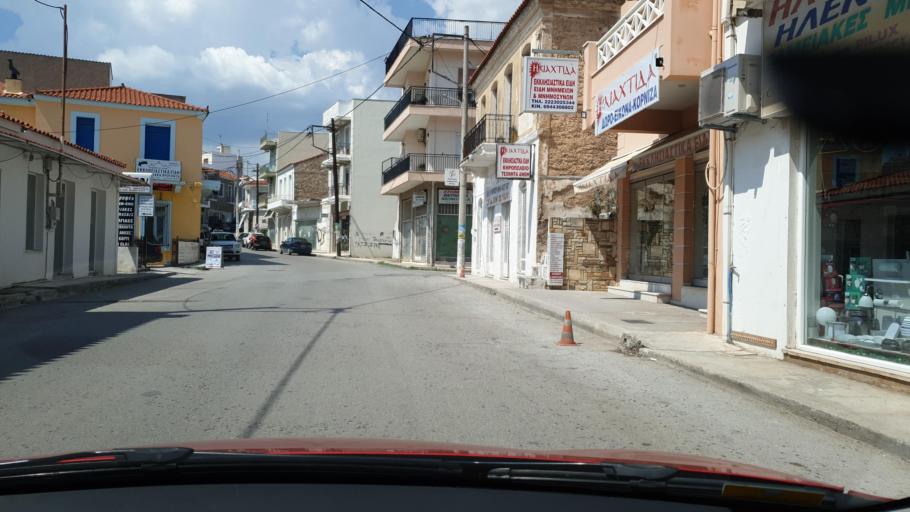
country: GR
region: Central Greece
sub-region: Nomos Evvoias
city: Aliveri
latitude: 38.4084
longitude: 24.0400
